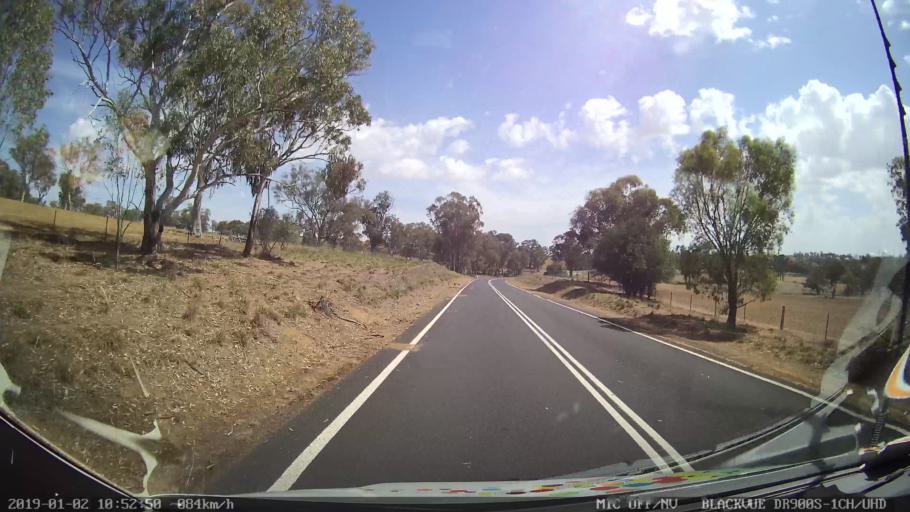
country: AU
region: New South Wales
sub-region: Cootamundra
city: Cootamundra
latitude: -34.6843
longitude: 148.2713
